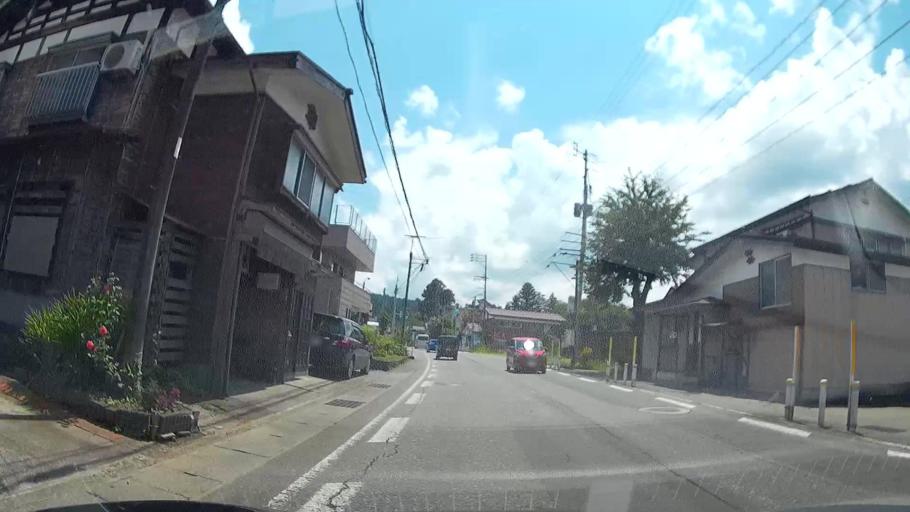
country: JP
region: Niigata
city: Tokamachi
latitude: 37.0741
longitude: 138.7155
